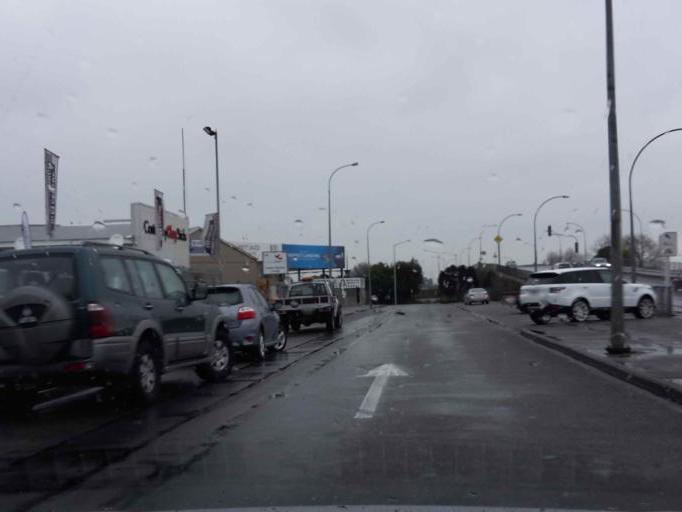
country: NZ
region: Canterbury
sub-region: Selwyn District
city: Prebbleton
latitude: -43.5402
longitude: 172.5521
